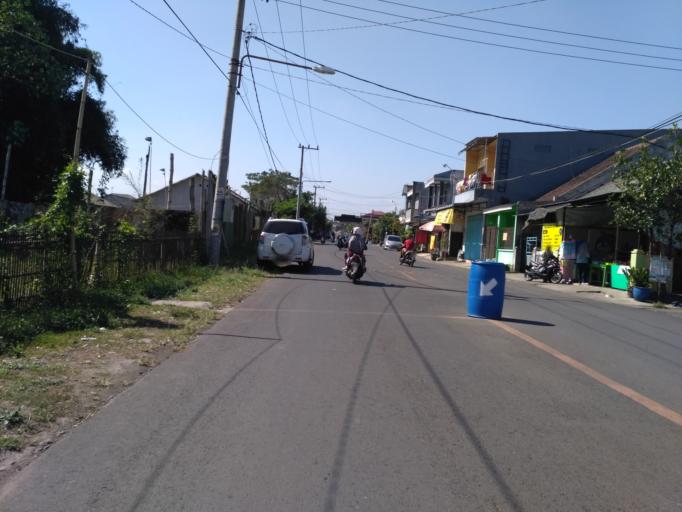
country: ID
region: East Java
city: Singosari
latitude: -7.9116
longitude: 112.6667
